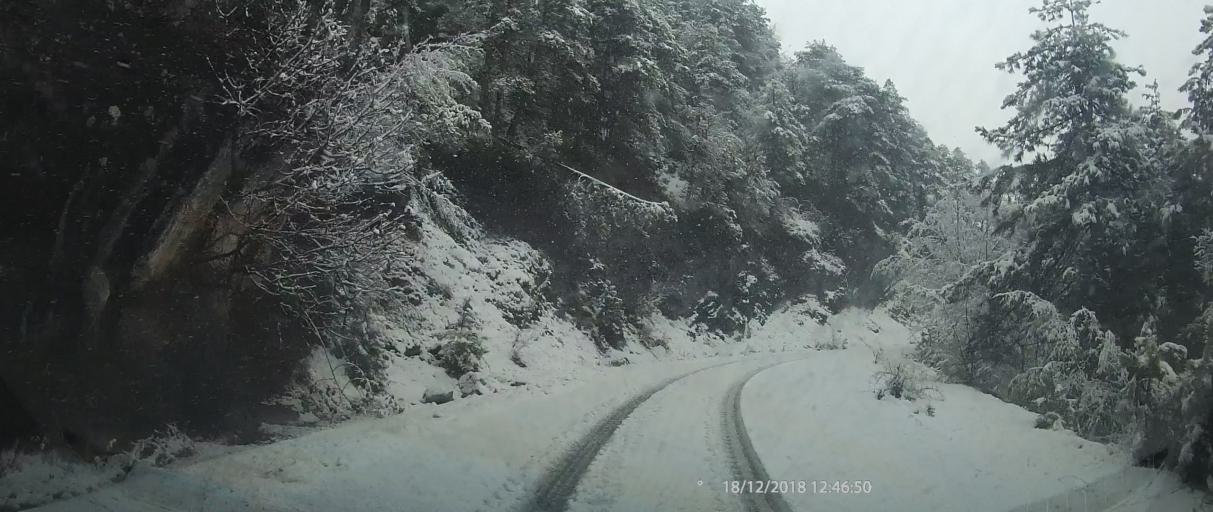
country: GR
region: Central Macedonia
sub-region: Nomos Pierias
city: Litochoro
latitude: 40.1001
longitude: 22.4346
